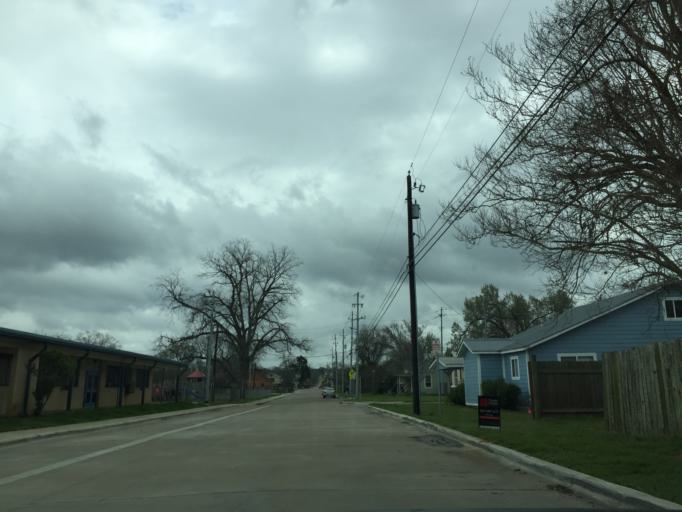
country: US
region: Texas
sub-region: Bastrop County
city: Bastrop
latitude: 30.1127
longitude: -97.3148
